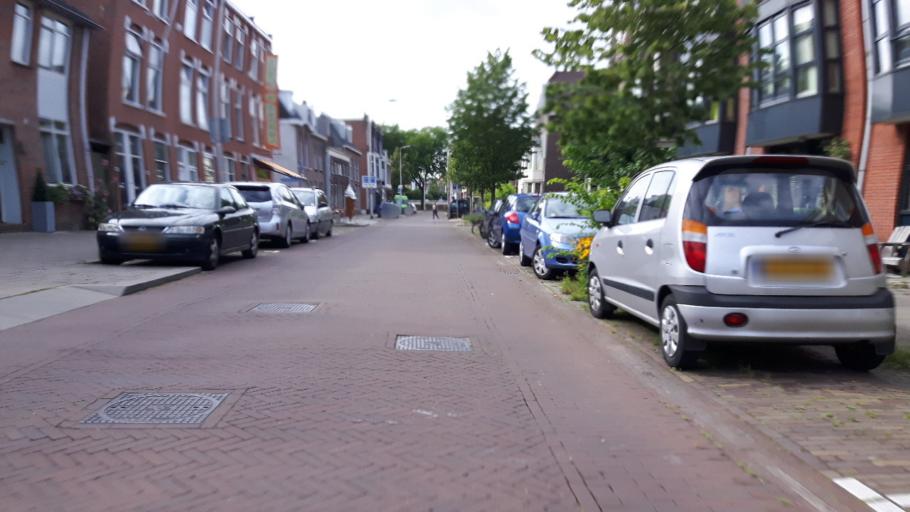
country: NL
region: South Holland
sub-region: Gemeente Delft
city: Delft
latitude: 52.0049
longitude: 4.3640
